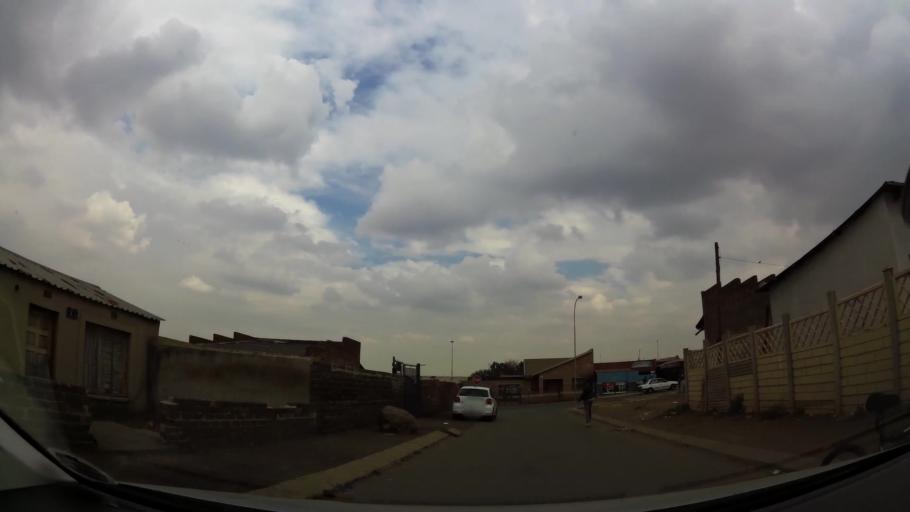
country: ZA
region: Gauteng
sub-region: City of Johannesburg Metropolitan Municipality
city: Soweto
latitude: -26.2627
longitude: 27.8632
